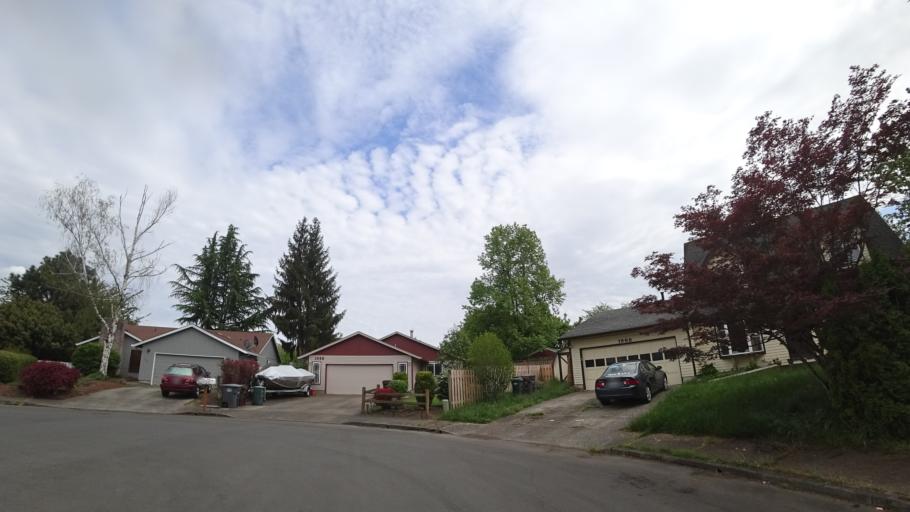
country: US
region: Oregon
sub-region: Washington County
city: Hillsboro
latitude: 45.4960
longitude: -122.9634
